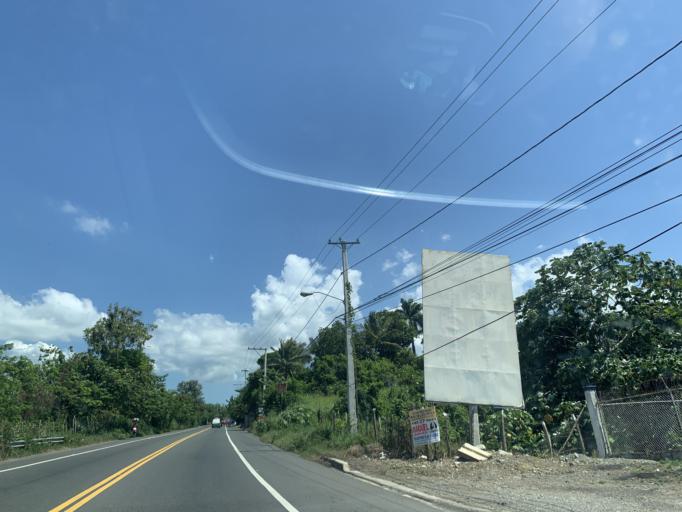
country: DO
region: Puerto Plata
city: Imbert
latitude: 19.7315
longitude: -70.8300
